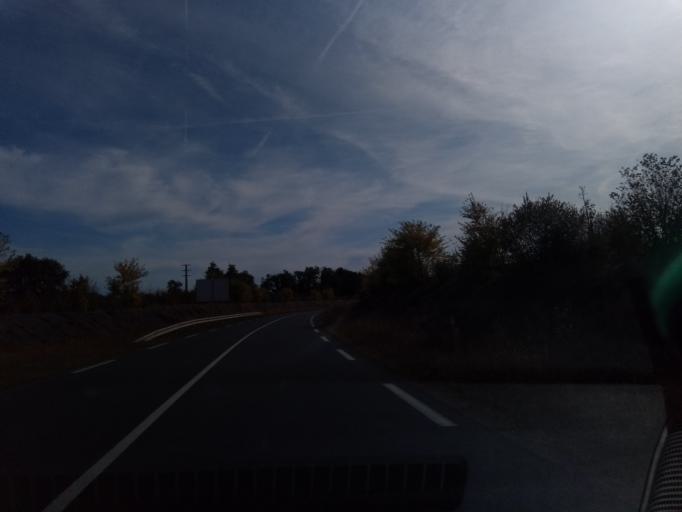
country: FR
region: Poitou-Charentes
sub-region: Departement de la Vienne
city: Saulge
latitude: 46.4092
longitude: 0.8952
